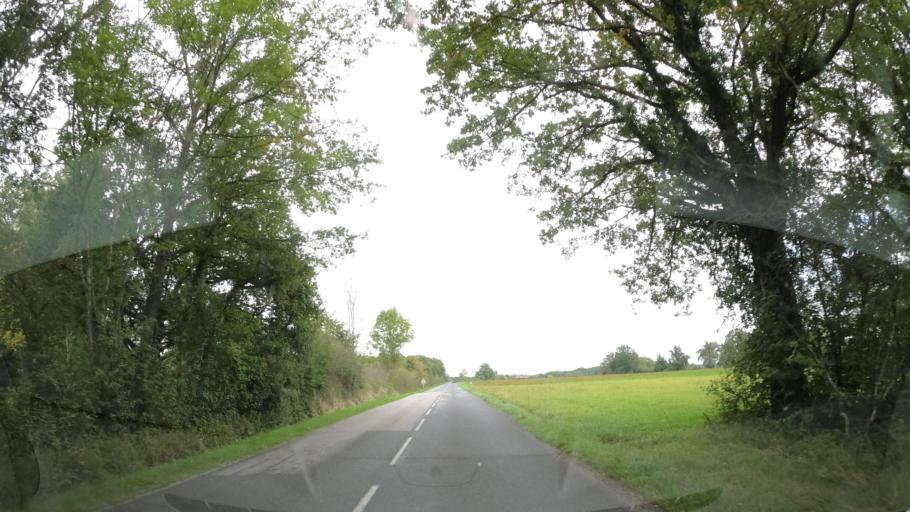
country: FR
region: Auvergne
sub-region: Departement de l'Allier
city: Saint-Gerand-le-Puy
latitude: 46.2796
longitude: 3.5543
